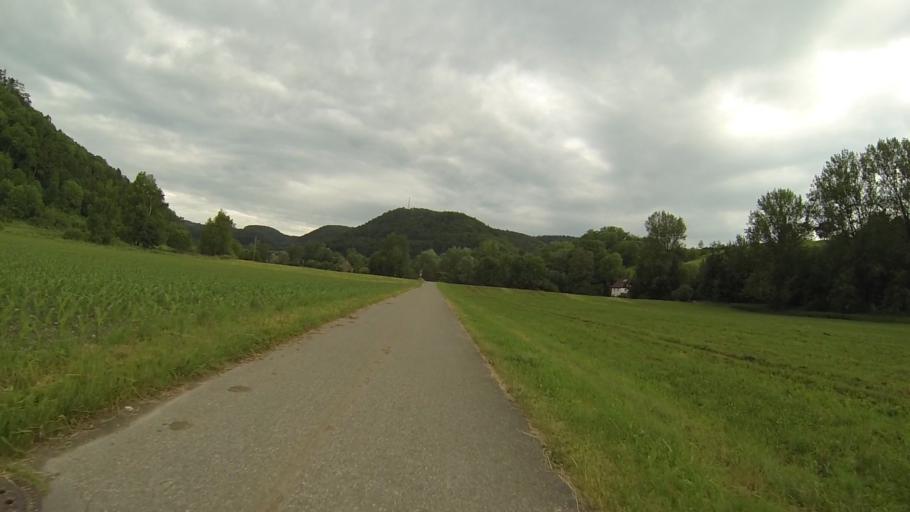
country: DE
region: Baden-Wuerttemberg
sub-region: Tuebingen Region
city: Blaubeuren
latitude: 48.4075
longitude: 9.7975
